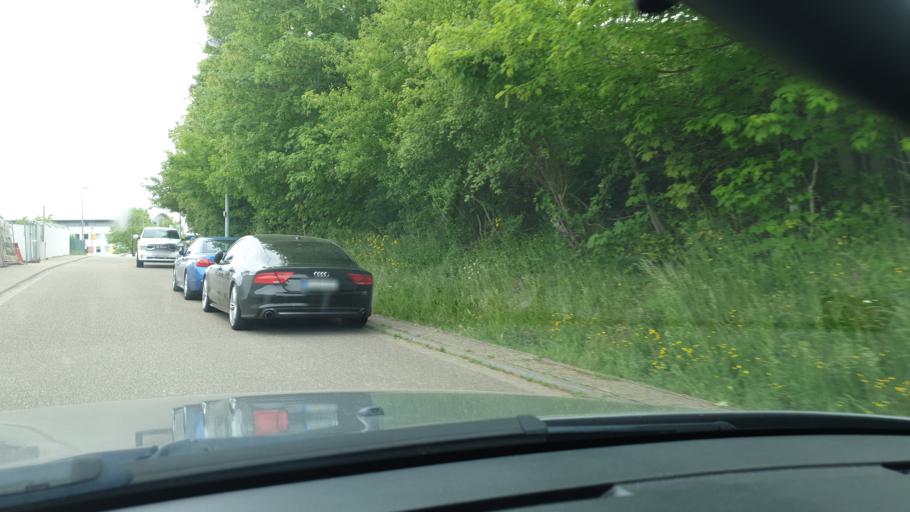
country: DE
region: Rheinland-Pfalz
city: Zweibrucken
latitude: 49.2599
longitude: 7.3618
